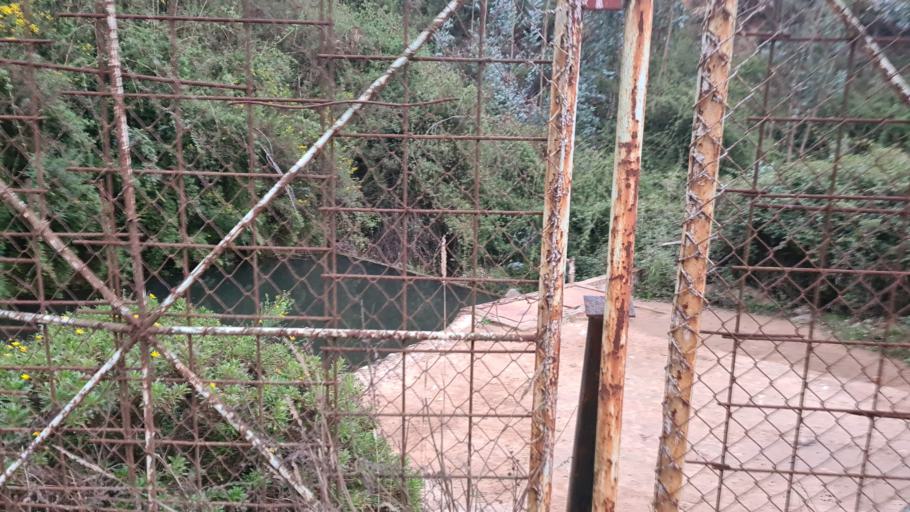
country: CL
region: Biobio
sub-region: Provincia de Concepcion
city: Penco
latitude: -36.7183
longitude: -72.9659
